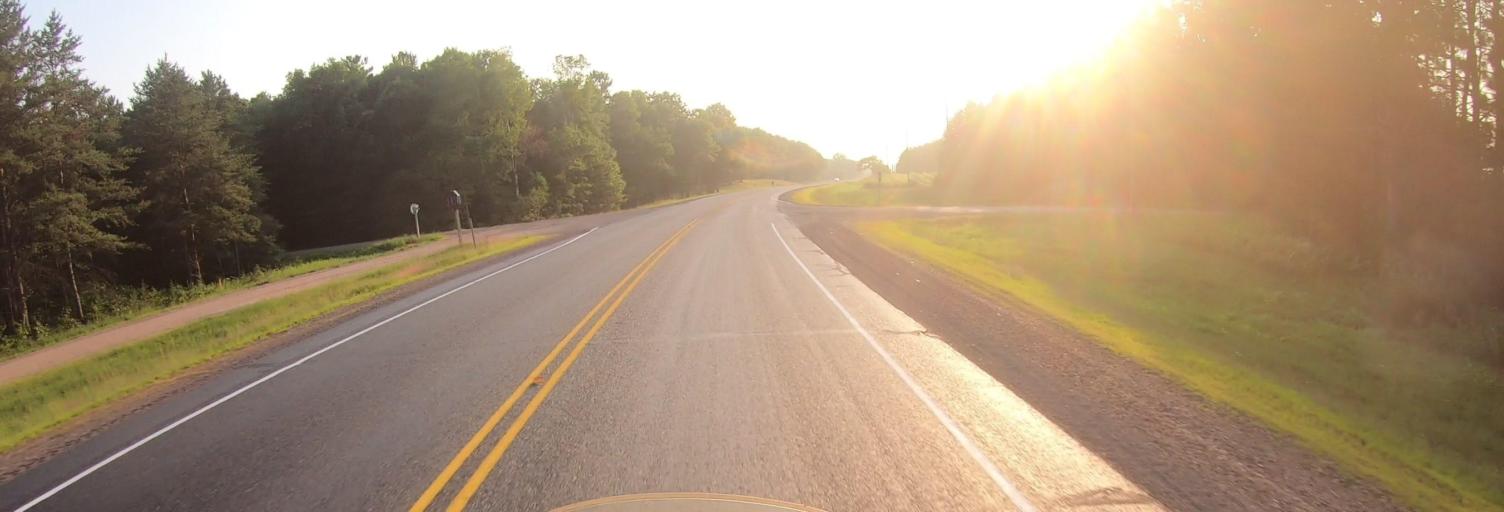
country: US
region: Wisconsin
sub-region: Washburn County
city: Spooner
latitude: 45.8155
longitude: -91.9695
